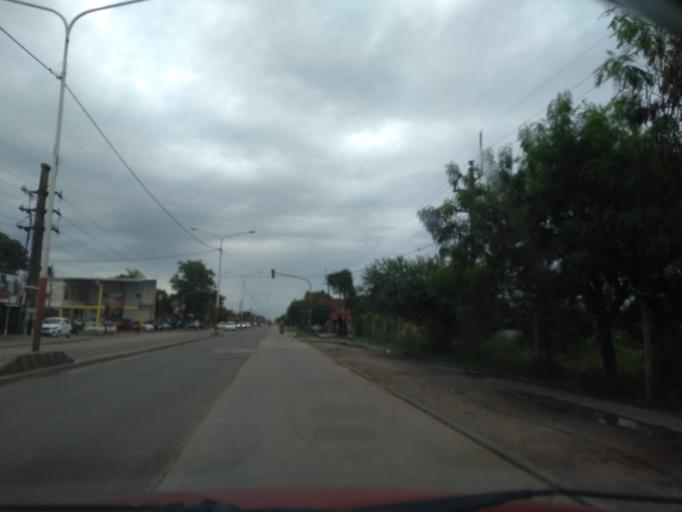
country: AR
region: Chaco
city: Barranqueras
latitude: -27.4833
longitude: -58.9644
